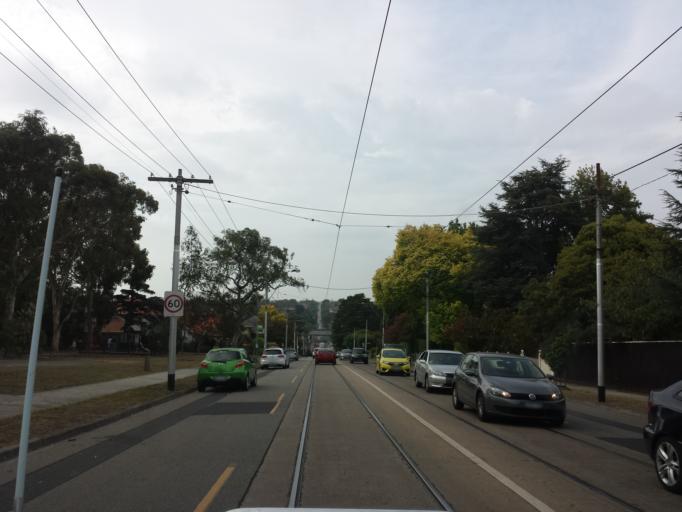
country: AU
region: Victoria
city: Toorak
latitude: -37.8429
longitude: 145.0317
